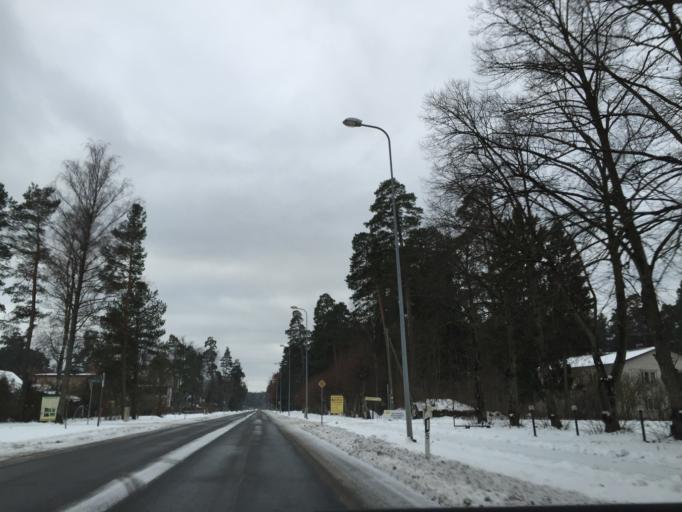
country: LV
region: Saulkrastu
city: Saulkrasti
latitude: 57.2426
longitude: 24.4012
